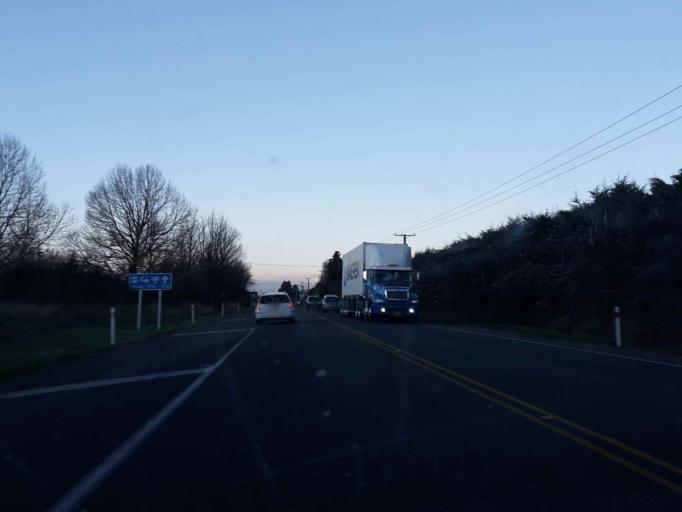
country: NZ
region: Canterbury
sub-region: Selwyn District
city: Prebbleton
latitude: -43.5564
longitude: 172.4696
